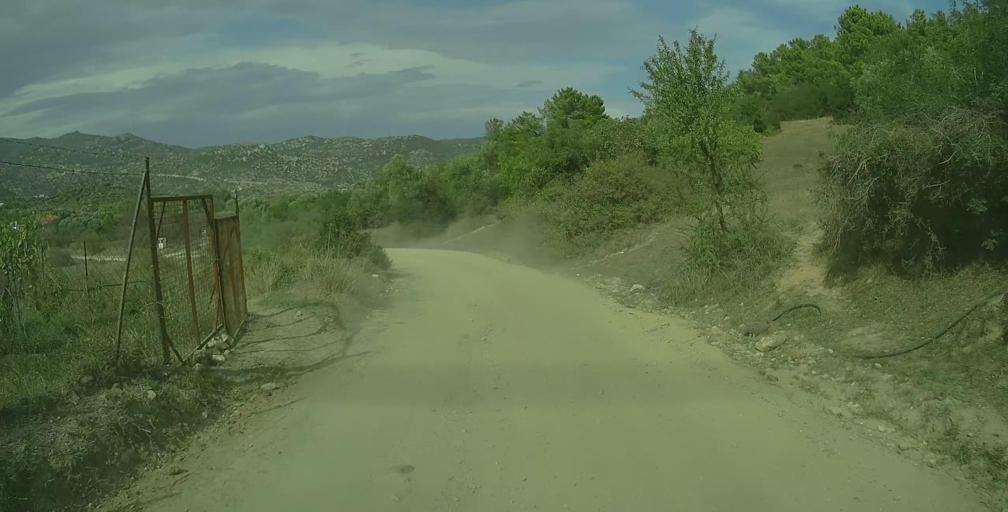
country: GR
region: Central Macedonia
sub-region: Nomos Chalkidikis
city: Sykia
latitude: 40.0257
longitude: 23.9463
